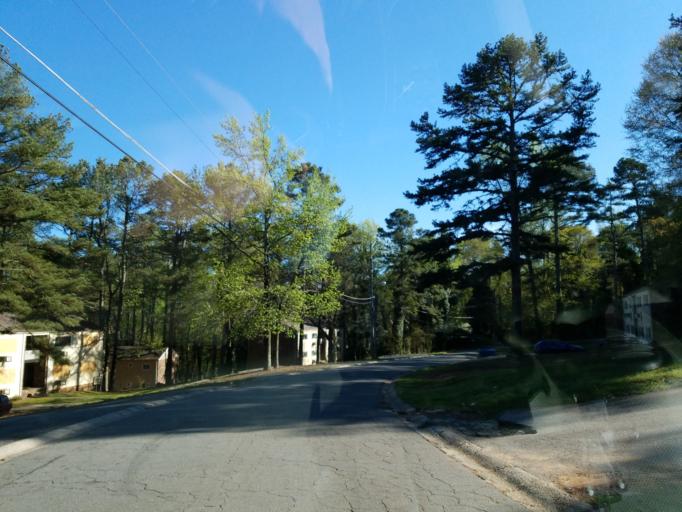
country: US
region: Georgia
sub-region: Cobb County
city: Marietta
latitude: 33.9630
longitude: -84.5048
